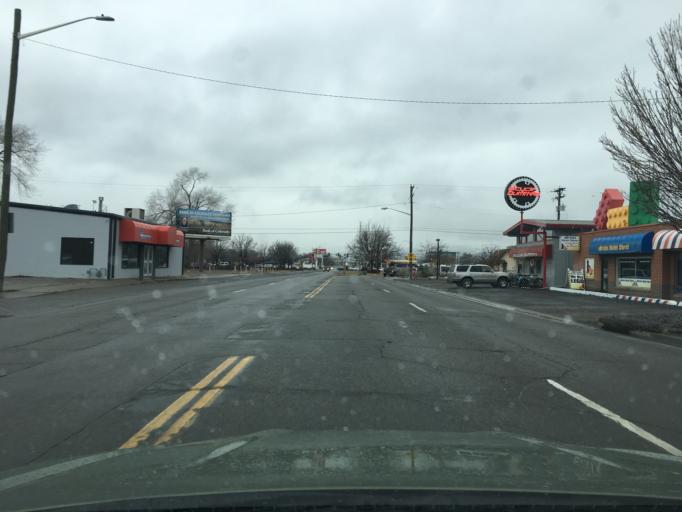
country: US
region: Colorado
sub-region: Mesa County
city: Grand Junction
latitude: 39.0725
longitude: -108.5708
